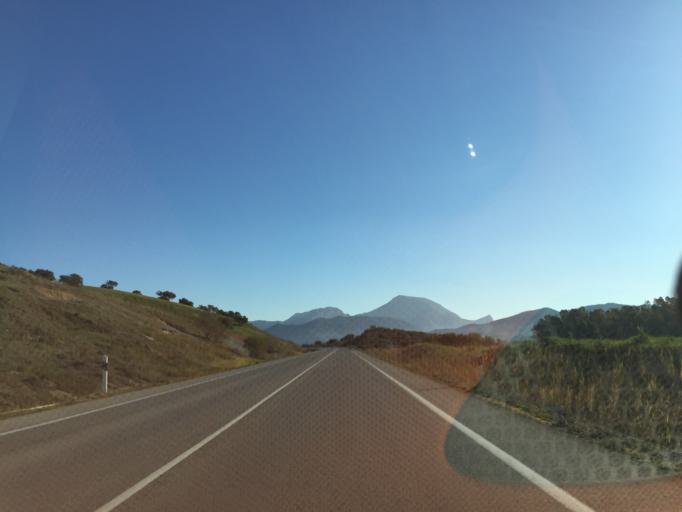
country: ES
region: Andalusia
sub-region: Provincia de Malaga
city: Ardales
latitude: 36.8976
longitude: -4.8463
